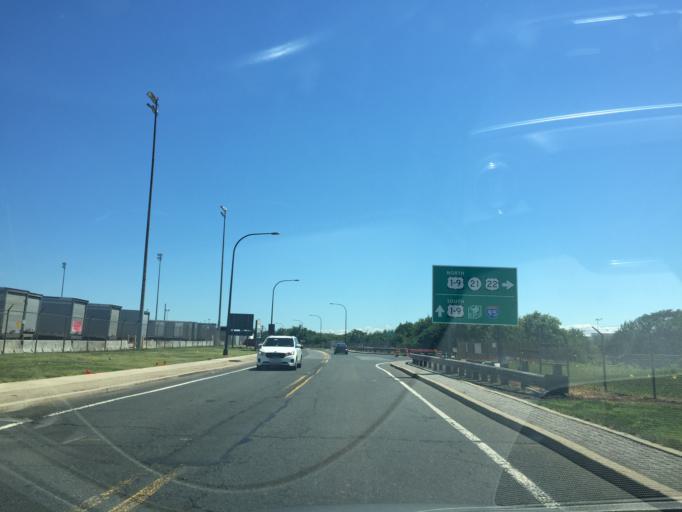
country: US
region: New Jersey
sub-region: Union County
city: Elizabeth
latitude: 40.6819
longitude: -74.1894
